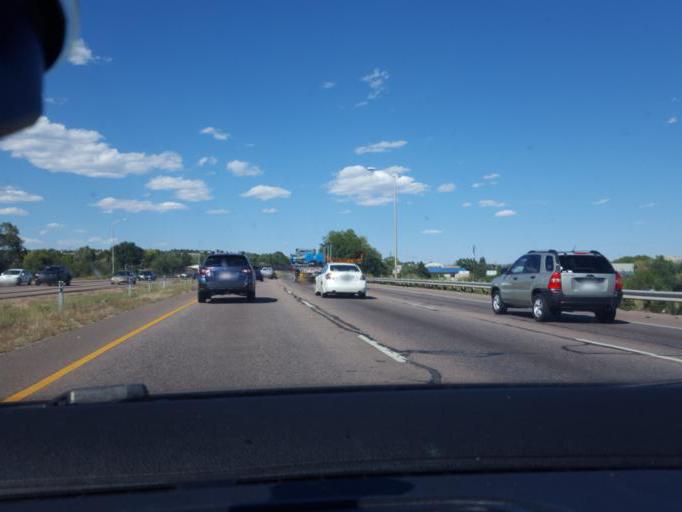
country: US
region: Colorado
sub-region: El Paso County
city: Colorado Springs
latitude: 38.8819
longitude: -104.8359
